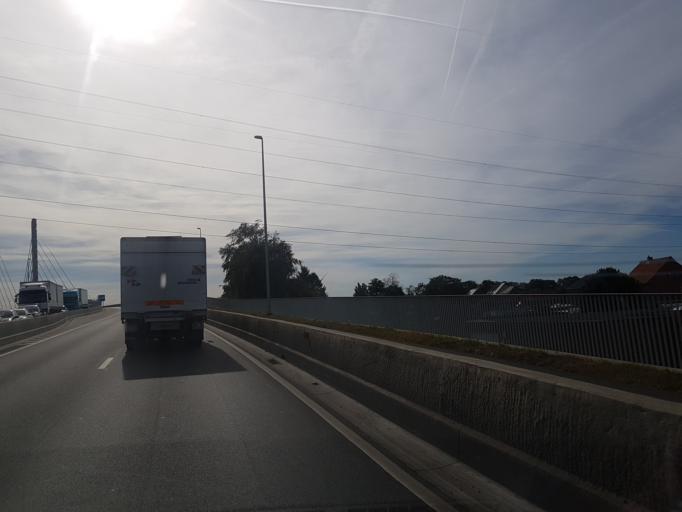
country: BE
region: Flanders
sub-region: Provincie Antwerpen
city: Westerlo
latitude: 51.1392
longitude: 4.9409
